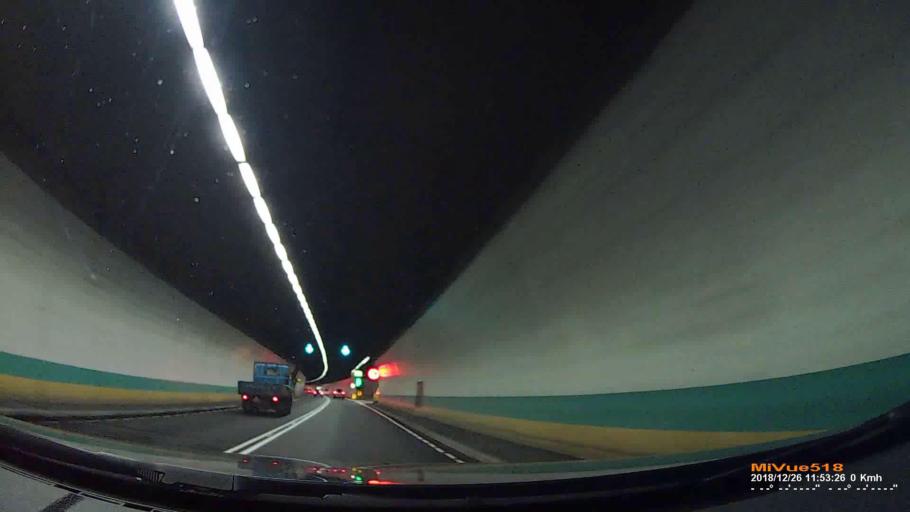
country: TW
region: Taiwan
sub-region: Keelung
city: Keelung
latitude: 24.9585
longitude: 121.6925
